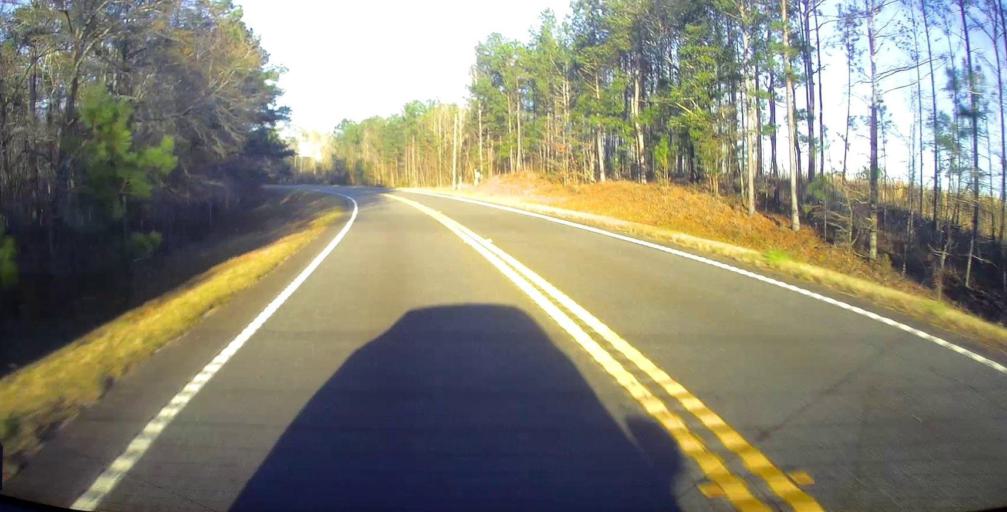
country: US
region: Georgia
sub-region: Talbot County
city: Talbotton
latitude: 32.6653
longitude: -84.6199
